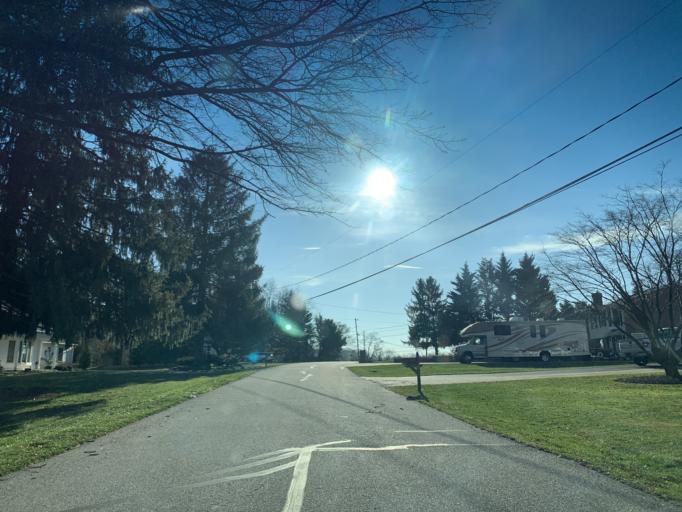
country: US
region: Maryland
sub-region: Harford County
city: Bel Air South
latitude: 39.5576
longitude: -76.2651
